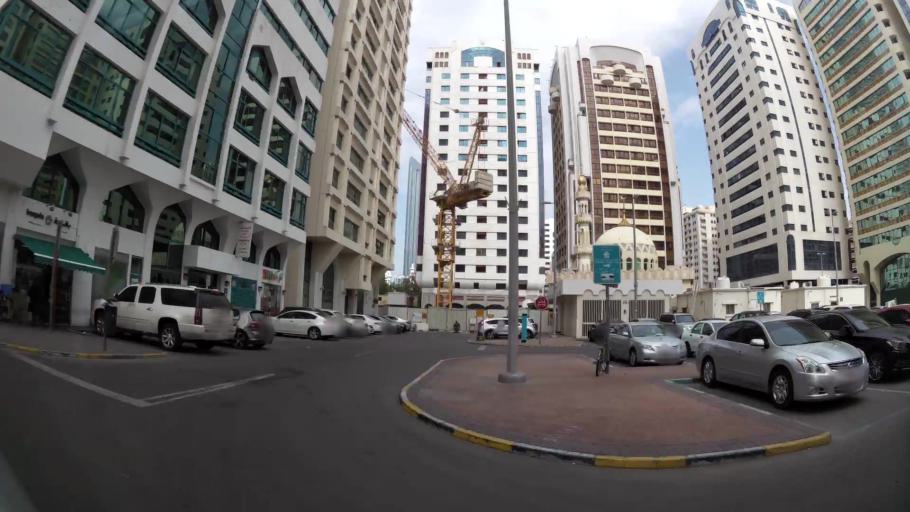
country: AE
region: Abu Dhabi
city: Abu Dhabi
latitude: 24.4808
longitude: 54.3503
